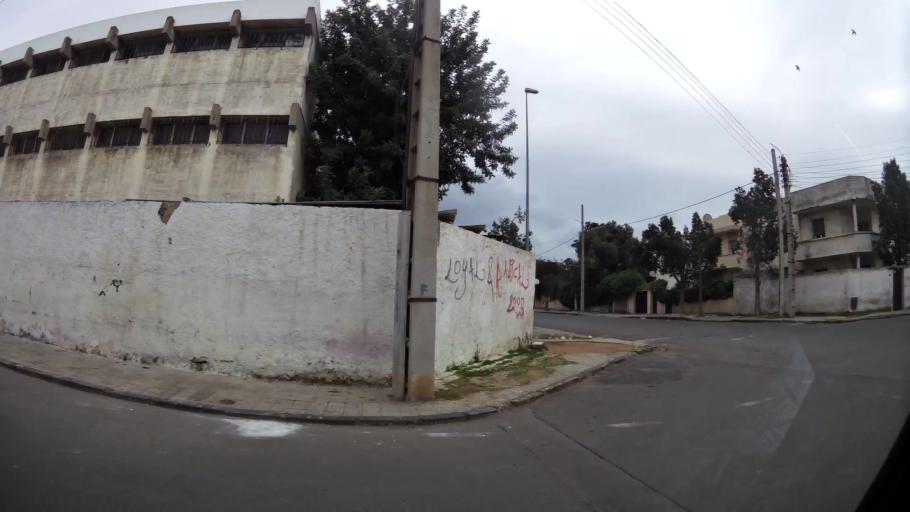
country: MA
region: Grand Casablanca
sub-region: Casablanca
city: Casablanca
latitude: 33.5925
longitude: -7.6478
